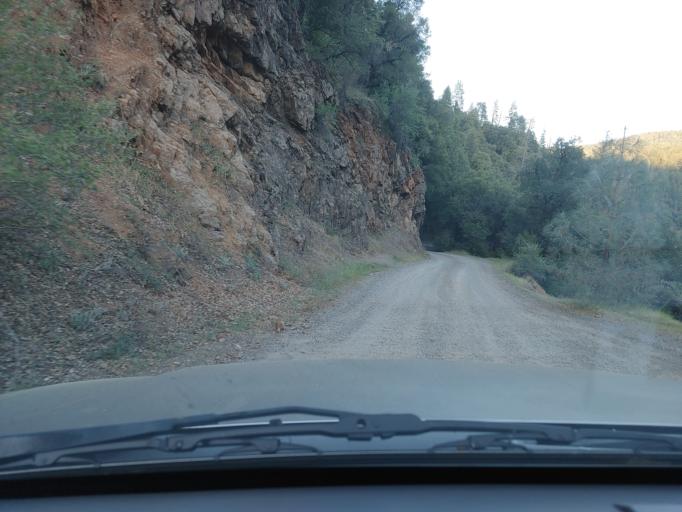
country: US
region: California
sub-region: Shasta County
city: Bella Vista
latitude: 40.8389
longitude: -122.0267
